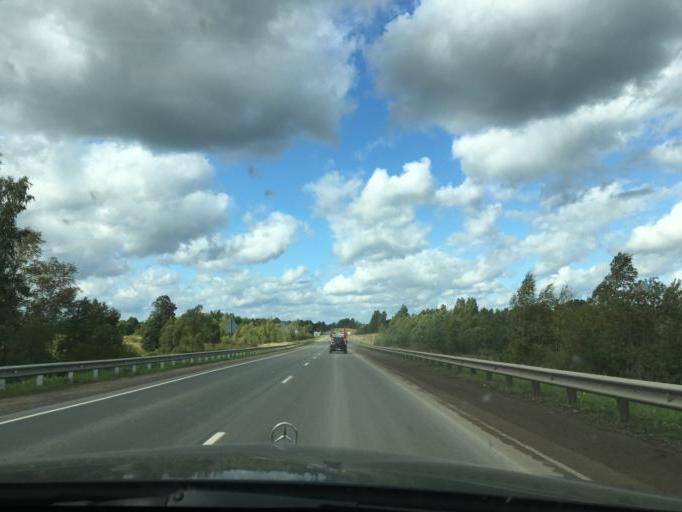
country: RU
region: Pskov
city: Novosokol'niki
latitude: 56.2964
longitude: 30.2274
